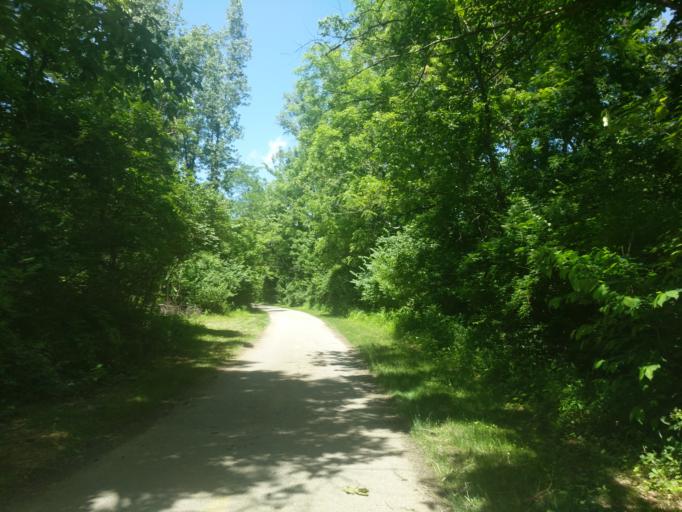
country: US
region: Ohio
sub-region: Franklin County
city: Minerva Park
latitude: 40.0609
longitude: -82.9245
